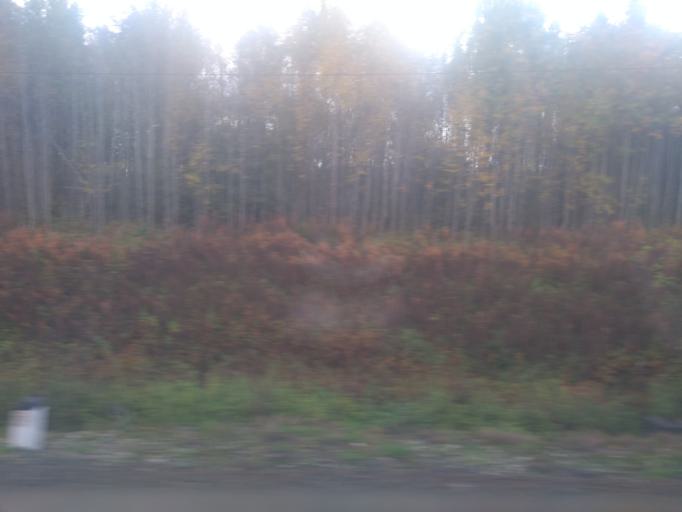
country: RU
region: Udmurtiya
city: Mozhga
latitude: 56.4264
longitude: 52.0556
